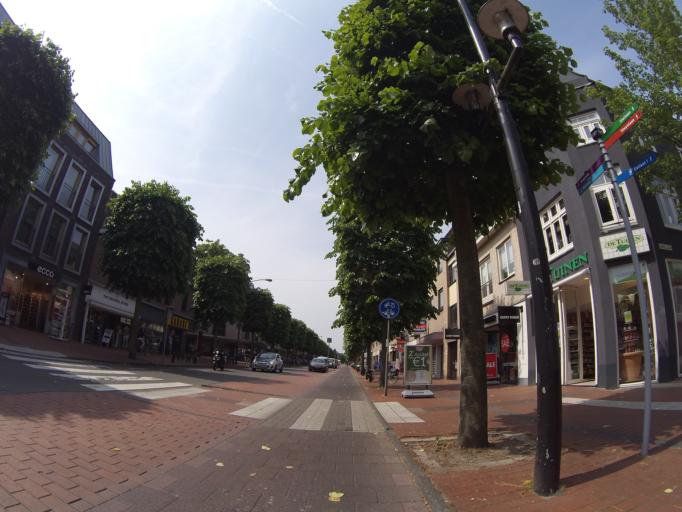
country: NL
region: Utrecht
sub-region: Gemeente Zeist
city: Zeist
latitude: 52.0867
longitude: 5.2456
